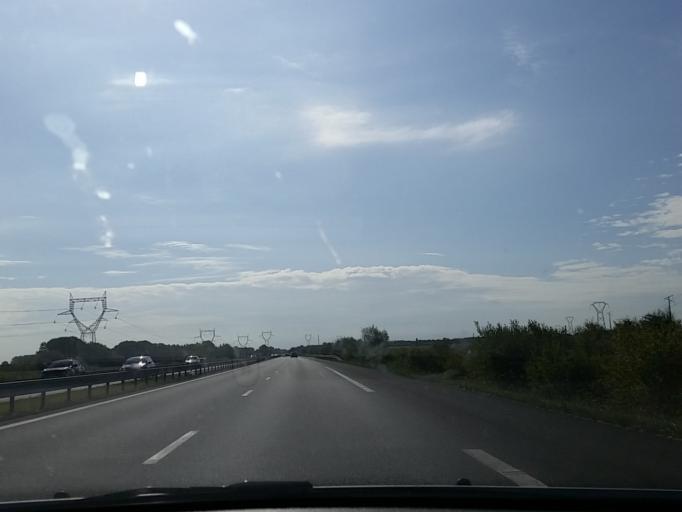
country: FR
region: Centre
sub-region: Departement du Cher
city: Marmagne
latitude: 47.0672
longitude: 2.2887
